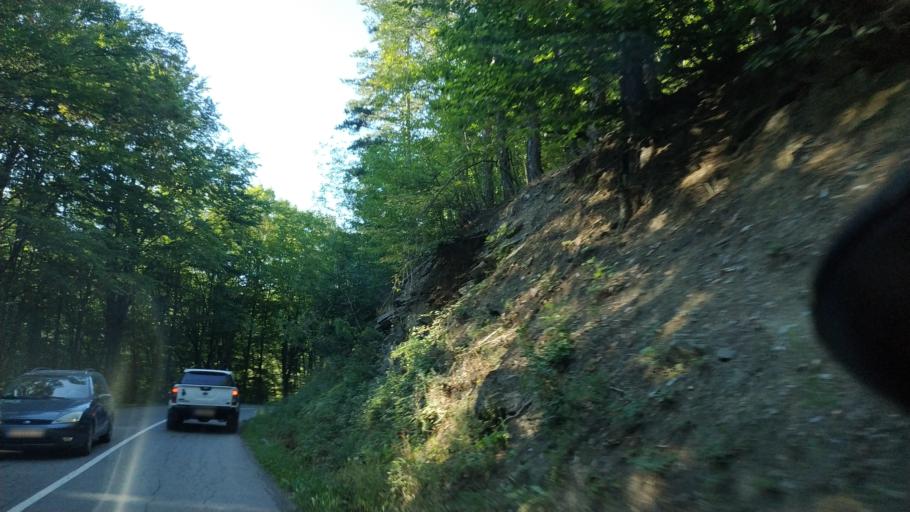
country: RS
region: Central Serbia
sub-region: Rasinski Okrug
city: Krusevac
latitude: 43.4564
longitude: 21.3594
